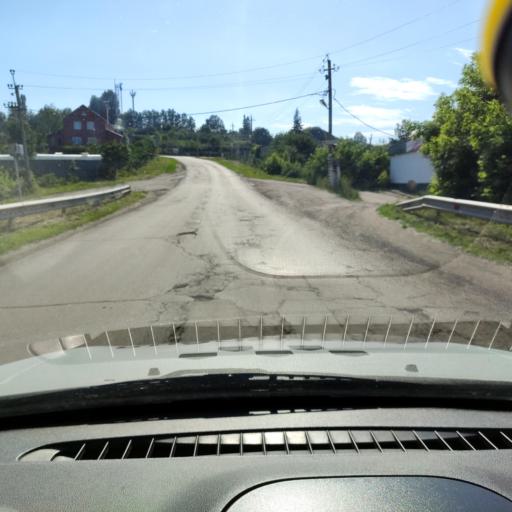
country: RU
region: Samara
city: Tol'yatti
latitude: 53.3562
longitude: 49.3051
